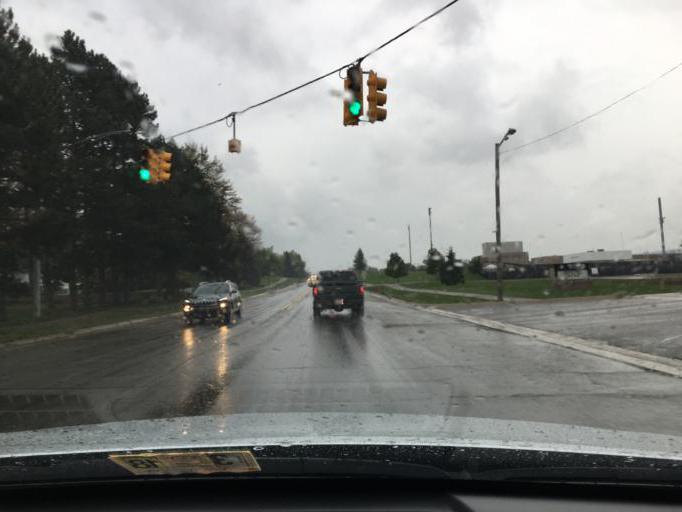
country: US
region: Michigan
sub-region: Oakland County
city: Auburn Hills
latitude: 42.6996
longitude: -83.1949
